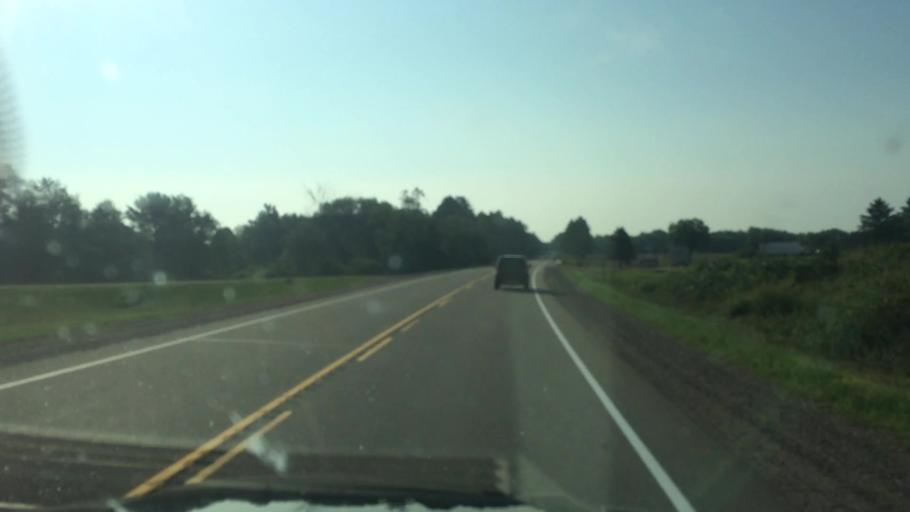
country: US
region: Wisconsin
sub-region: Langlade County
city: Antigo
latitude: 45.1462
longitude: -89.2474
